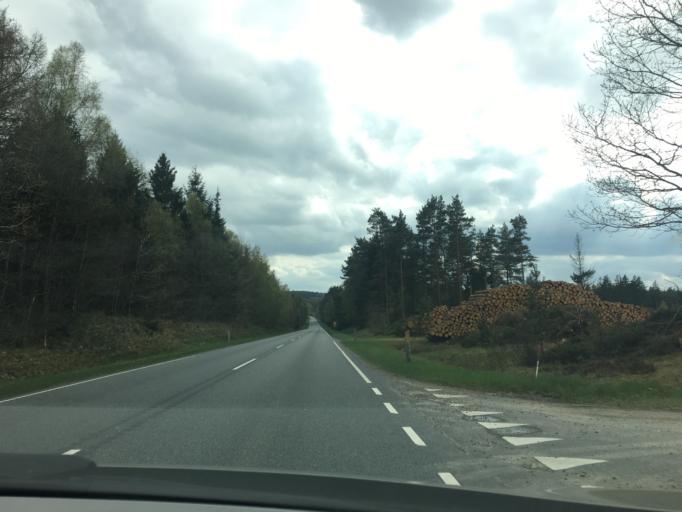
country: DK
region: Central Jutland
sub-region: Silkeborg Kommune
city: Virklund
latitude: 56.0660
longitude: 9.5799
